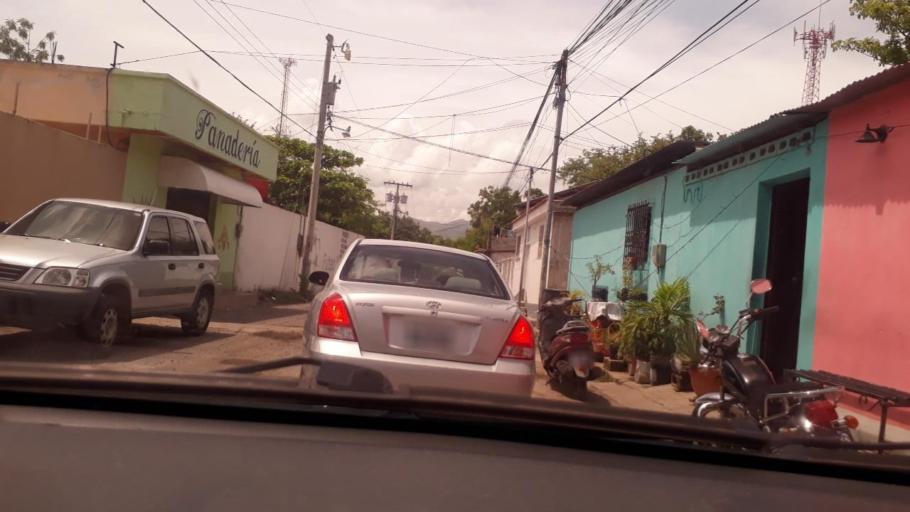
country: GT
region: Zacapa
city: Teculutan
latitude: 14.9933
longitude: -89.7226
